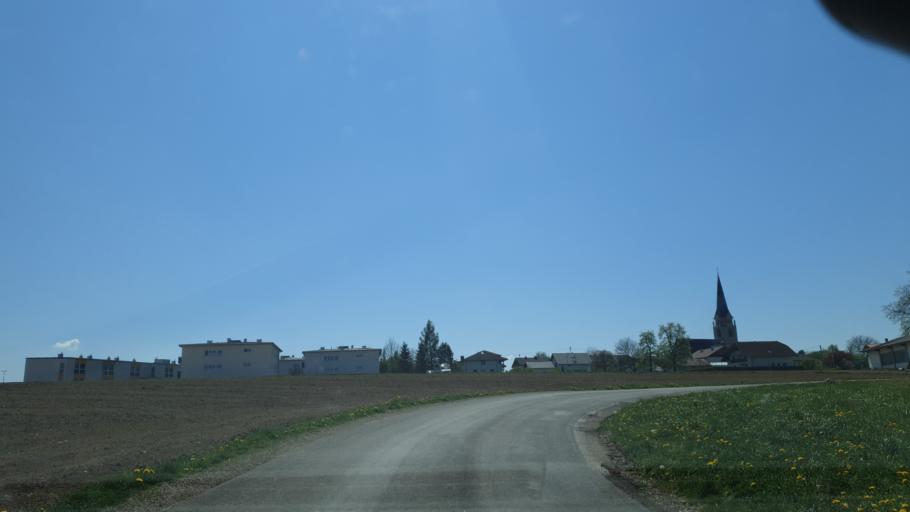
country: AT
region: Upper Austria
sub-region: Politischer Bezirk Vocklabruck
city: Gampern
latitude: 47.9920
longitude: 13.5584
